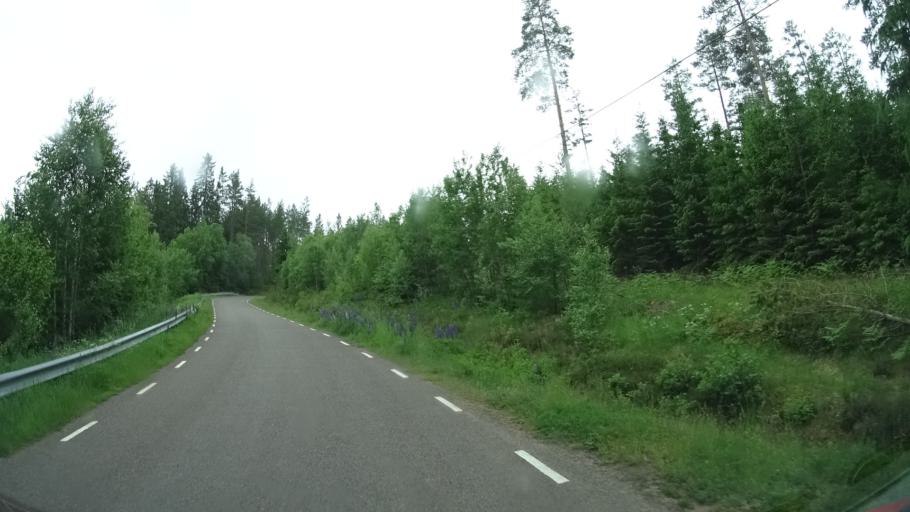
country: SE
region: Kalmar
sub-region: Vimmerby Kommun
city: Sodra Vi
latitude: 57.6981
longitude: 15.7299
